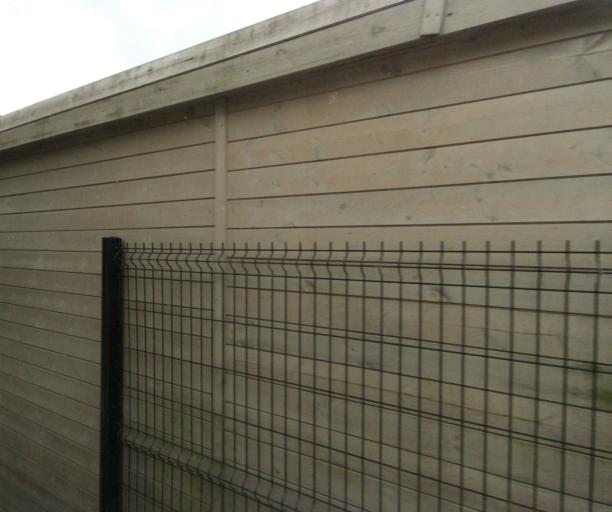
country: FR
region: Nord-Pas-de-Calais
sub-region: Departement du Nord
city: Neuville-en-Ferrain
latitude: 50.7690
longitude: 3.1623
